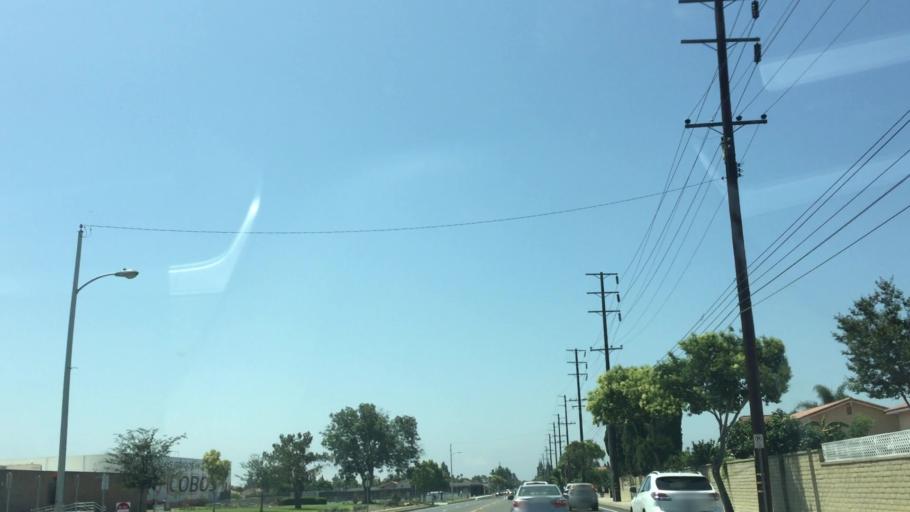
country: US
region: California
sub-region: Orange County
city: Fountain Valley
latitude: 33.7231
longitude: -117.9285
